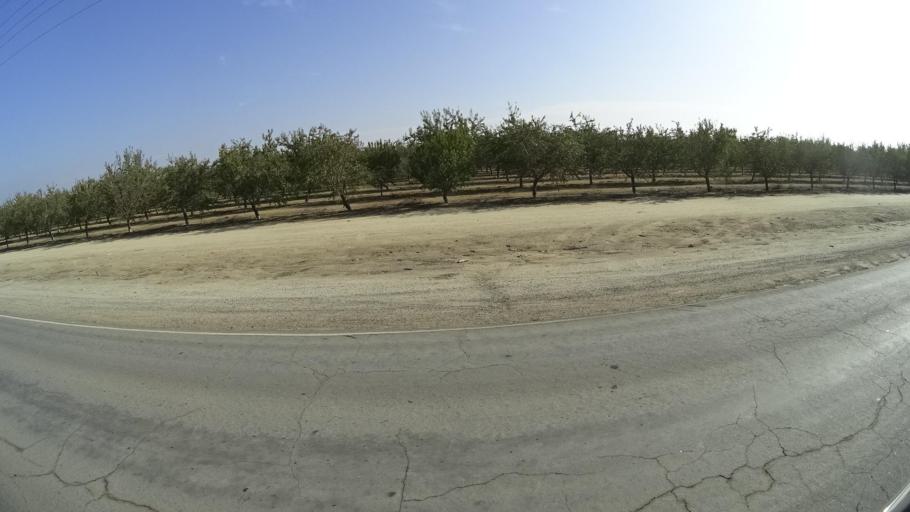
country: US
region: California
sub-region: Kern County
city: Delano
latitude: 35.7551
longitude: -119.2233
